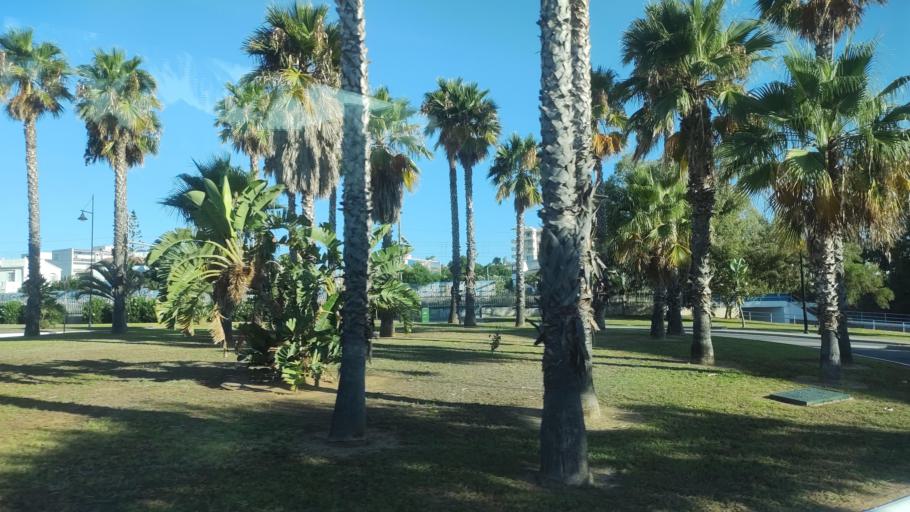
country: ES
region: Andalusia
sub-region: Provincia de Malaga
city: Torremolinos
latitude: 36.6436
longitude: -4.4857
